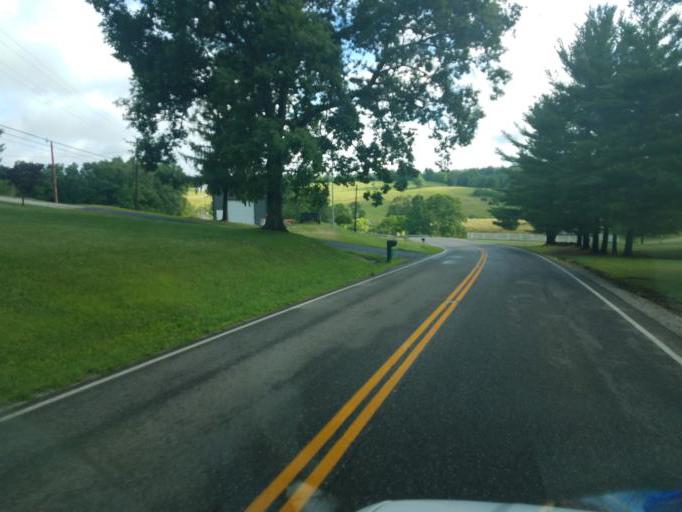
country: US
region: Ohio
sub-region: Jackson County
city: Oak Hill
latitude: 38.8041
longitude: -82.3994
